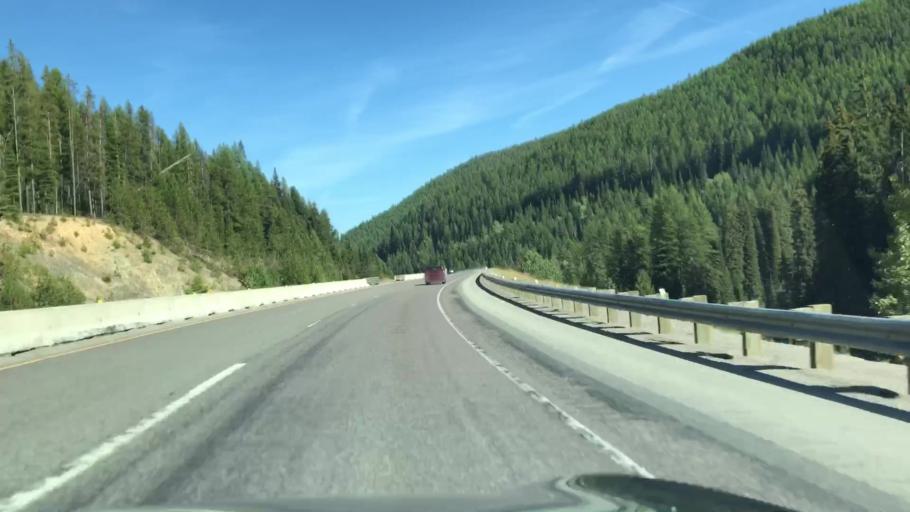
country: US
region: Montana
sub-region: Sanders County
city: Thompson Falls
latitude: 47.4164
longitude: -115.5804
